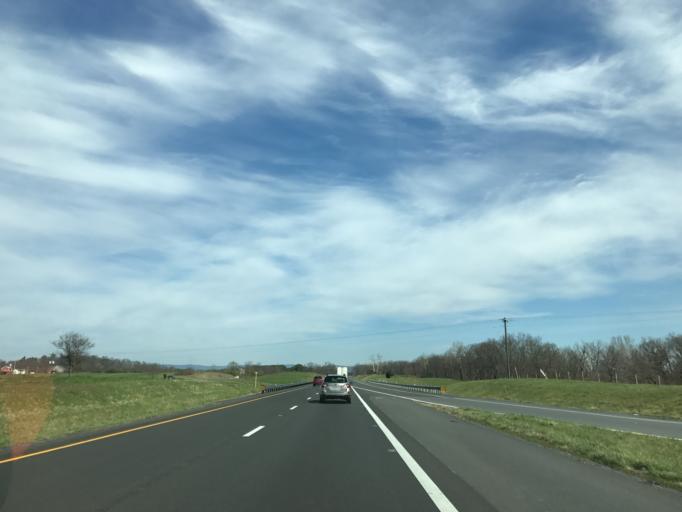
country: US
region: Virginia
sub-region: Shenandoah County
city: Mount Jackson
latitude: 38.7064
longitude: -78.6569
